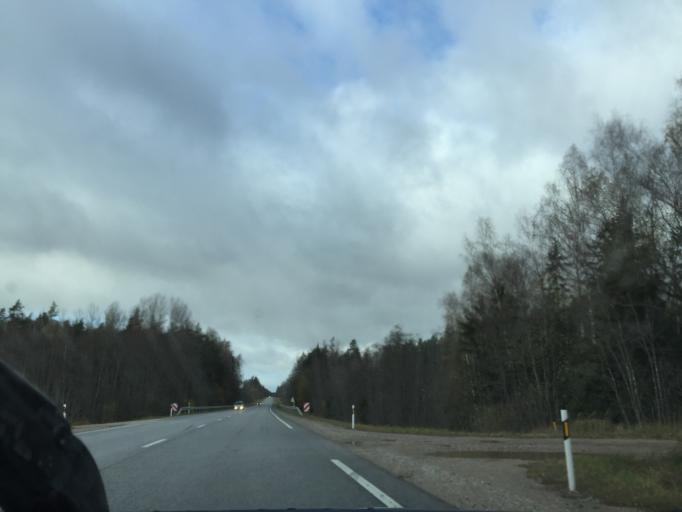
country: LV
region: Tukuma Rajons
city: Tukums
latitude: 56.9837
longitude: 23.0366
